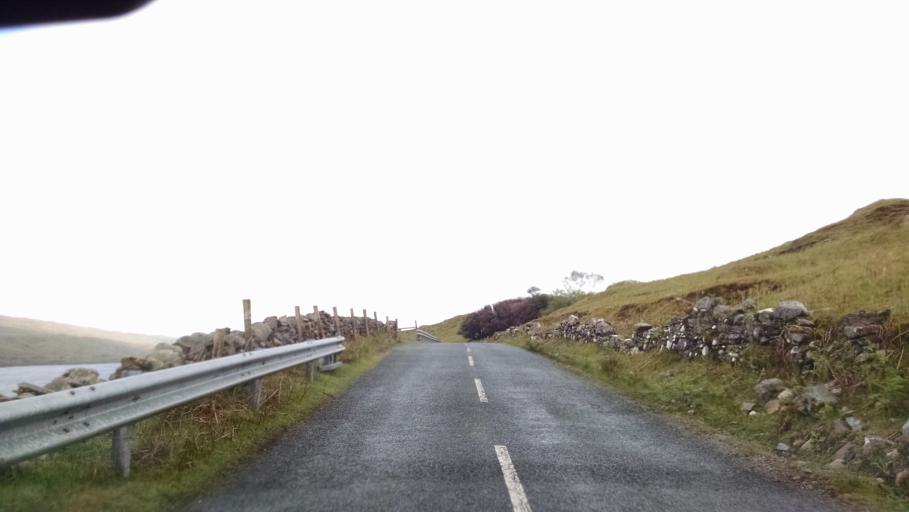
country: IE
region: Connaught
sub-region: Maigh Eo
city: Westport
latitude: 53.6042
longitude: -9.7287
